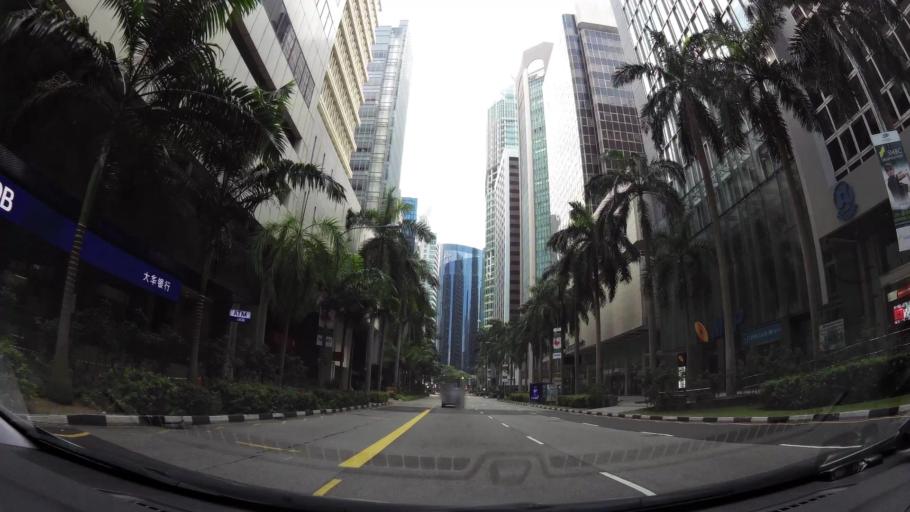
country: SG
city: Singapore
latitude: 1.2798
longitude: 103.8485
